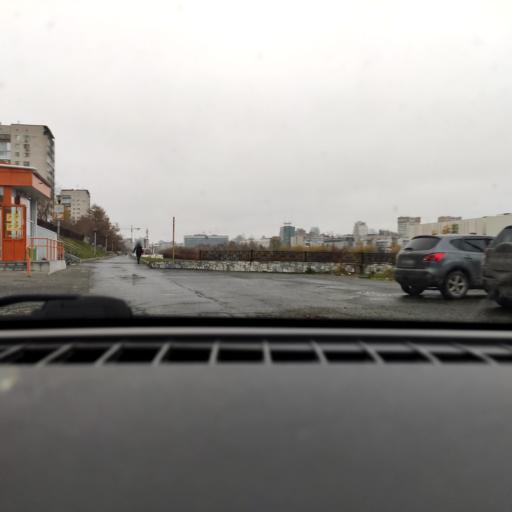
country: RU
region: Perm
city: Perm
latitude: 58.0090
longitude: 56.2124
